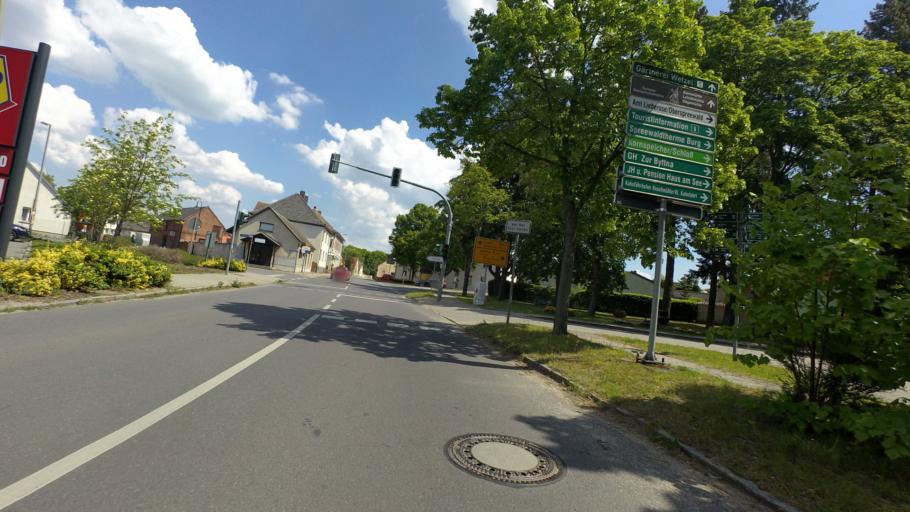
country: DE
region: Brandenburg
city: Straupitz
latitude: 51.9119
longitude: 14.1194
